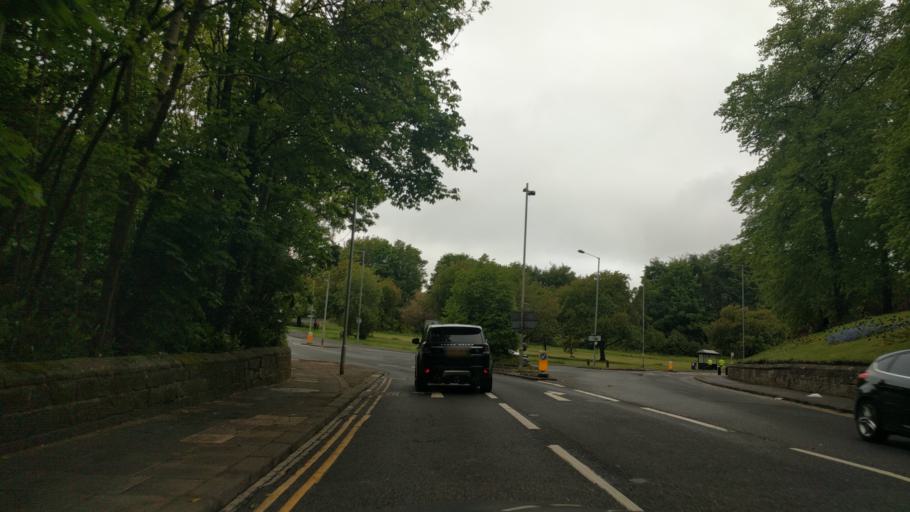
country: GB
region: England
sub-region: Northumberland
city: Morpeth
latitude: 55.1637
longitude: -1.6850
